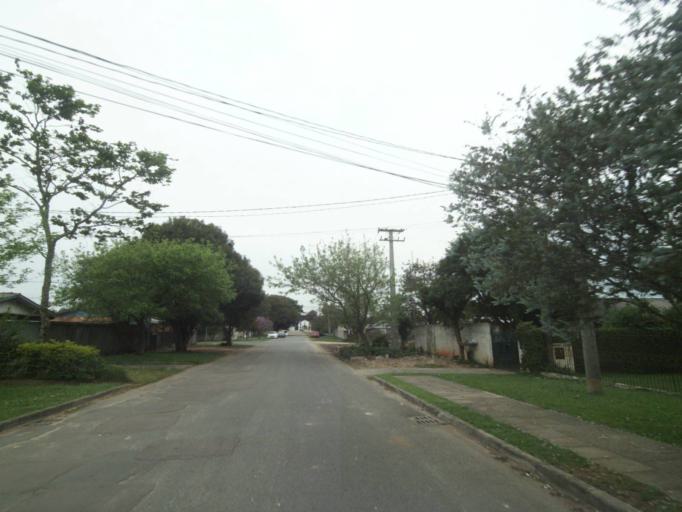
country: BR
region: Parana
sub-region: Pinhais
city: Pinhais
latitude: -25.4160
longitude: -49.1988
